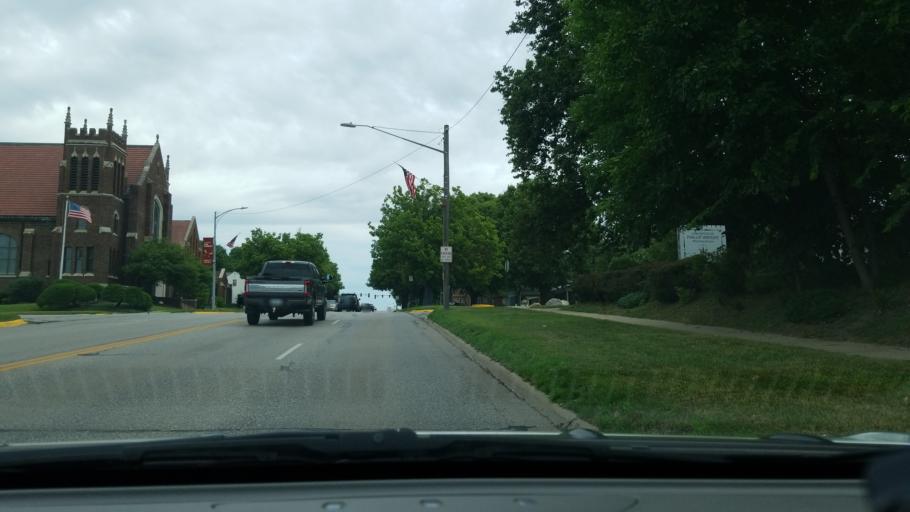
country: US
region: Nebraska
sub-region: Sarpy County
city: Papillion
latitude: 41.1591
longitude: -96.0429
